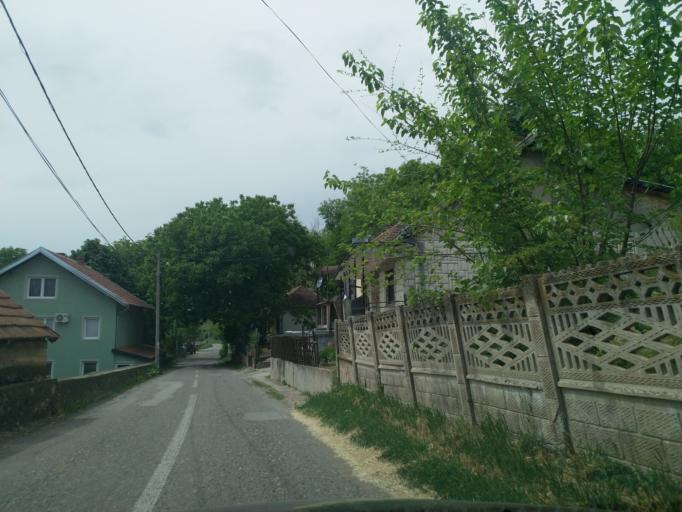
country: RS
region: Central Serbia
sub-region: Pomoravski Okrug
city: Paracin
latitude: 43.8629
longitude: 21.5867
